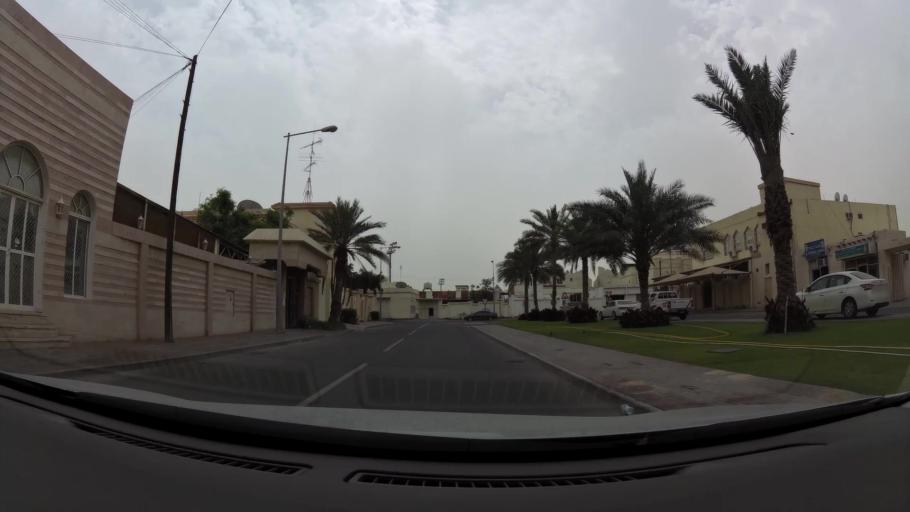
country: QA
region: Baladiyat ad Dawhah
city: Doha
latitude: 25.2619
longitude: 51.5163
